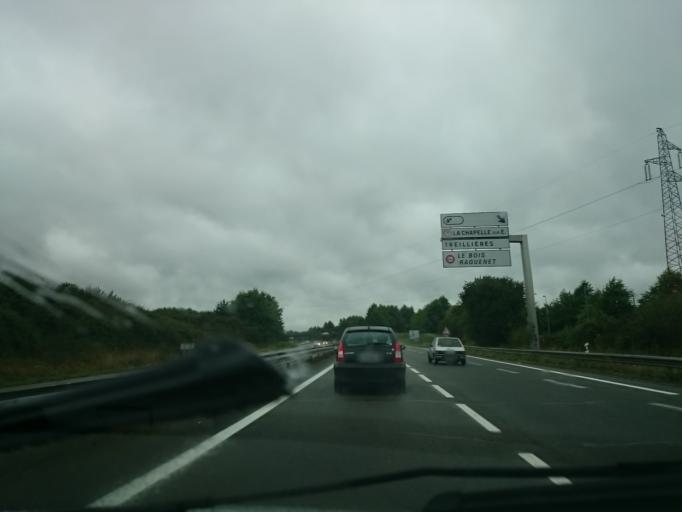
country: FR
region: Pays de la Loire
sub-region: Departement de la Loire-Atlantique
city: Orvault
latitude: 47.2752
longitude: -1.5951
